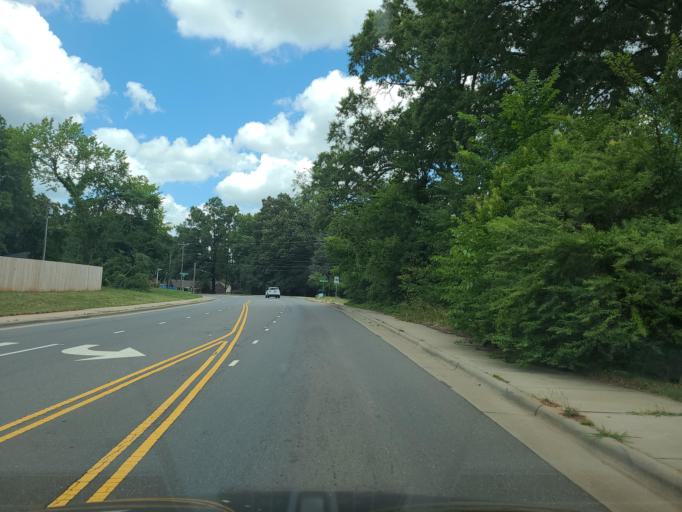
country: US
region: North Carolina
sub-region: Mecklenburg County
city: Charlotte
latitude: 35.2513
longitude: -80.8982
